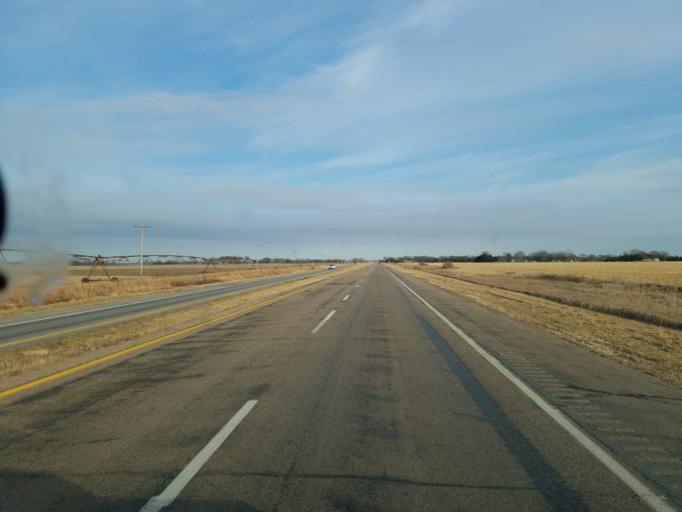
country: US
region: South Dakota
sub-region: Union County
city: Dakota Dunes
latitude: 42.4483
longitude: -96.5455
